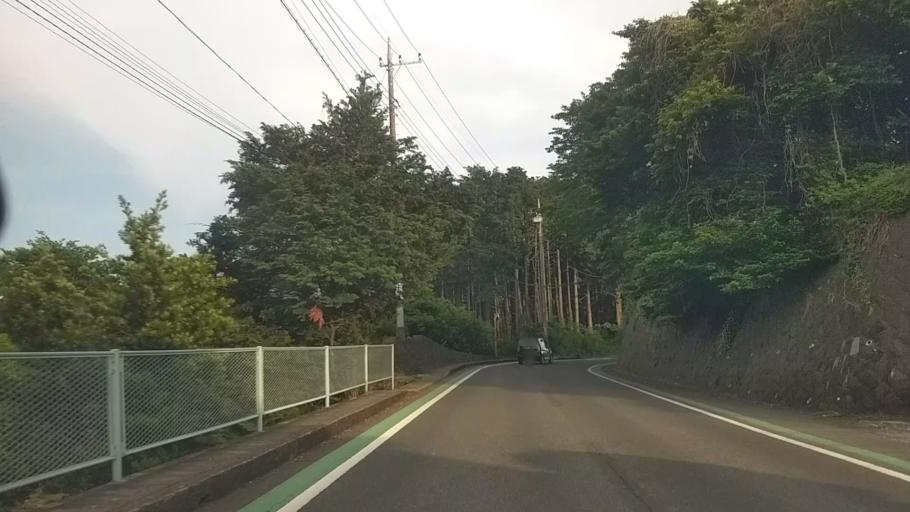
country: JP
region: Kanagawa
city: Odawara
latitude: 35.3259
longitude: 139.1076
